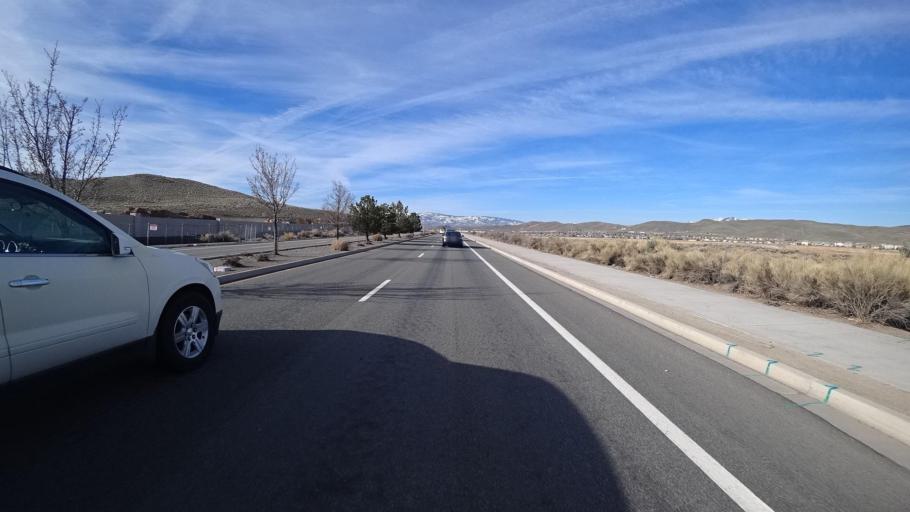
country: US
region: Nevada
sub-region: Washoe County
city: Spanish Springs
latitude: 39.6020
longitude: -119.7094
